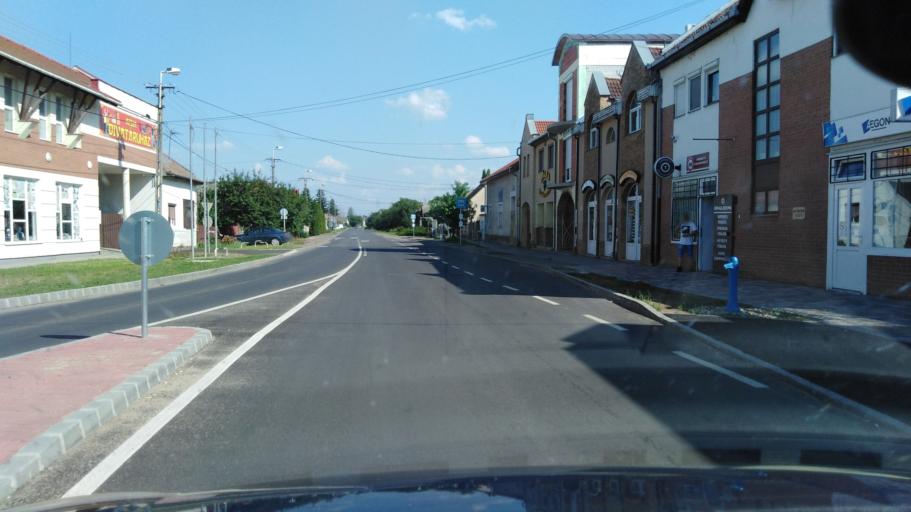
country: HU
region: Szabolcs-Szatmar-Bereg
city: Nyirbator
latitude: 47.8332
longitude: 22.1346
